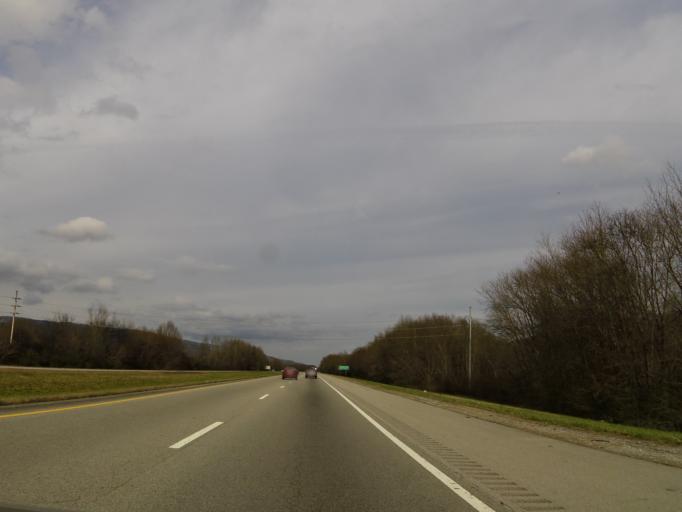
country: US
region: Tennessee
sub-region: Hamilton County
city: Falling Water
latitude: 35.1982
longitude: -85.2351
